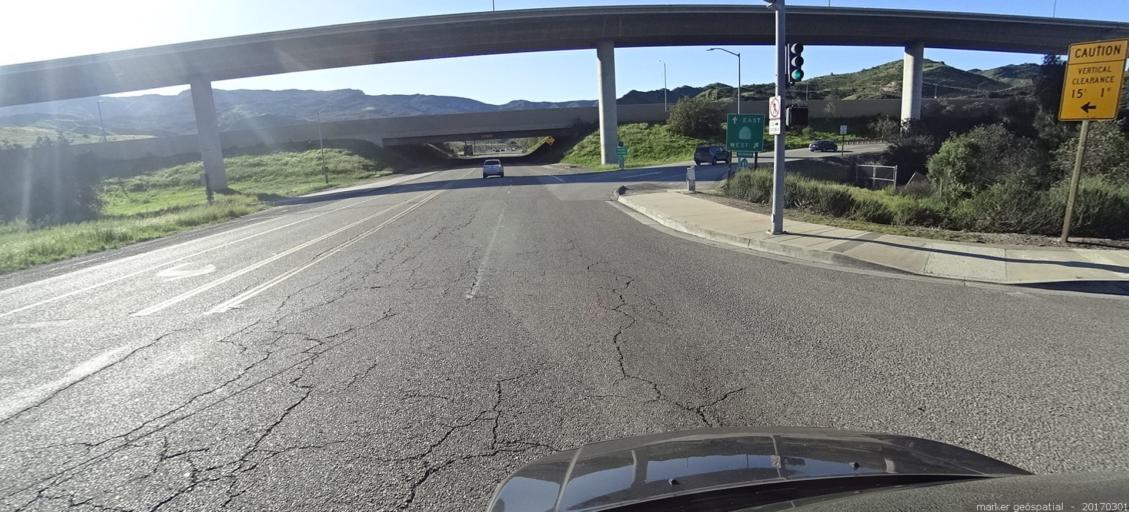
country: US
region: California
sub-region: Orange County
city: Yorba Linda
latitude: 33.8681
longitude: -117.7122
